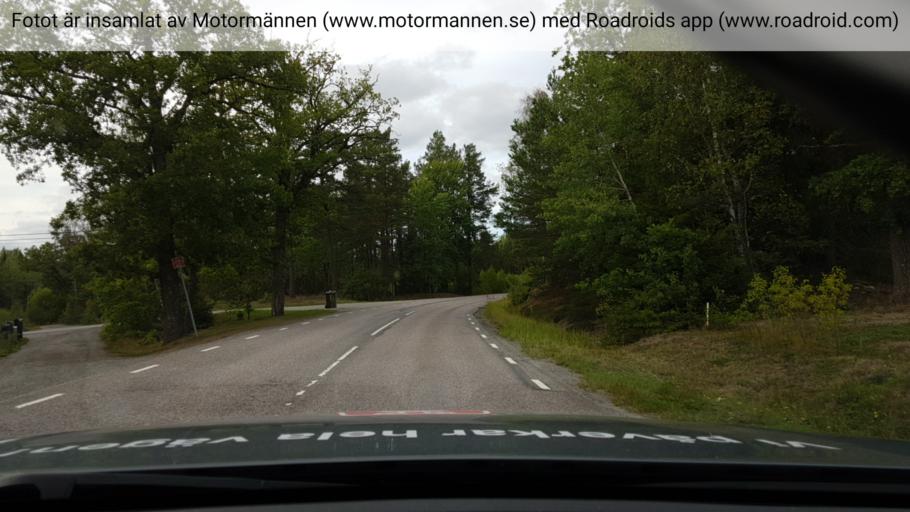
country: SE
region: Stockholm
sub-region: Haninge Kommun
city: Haninge
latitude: 59.1216
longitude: 18.1854
